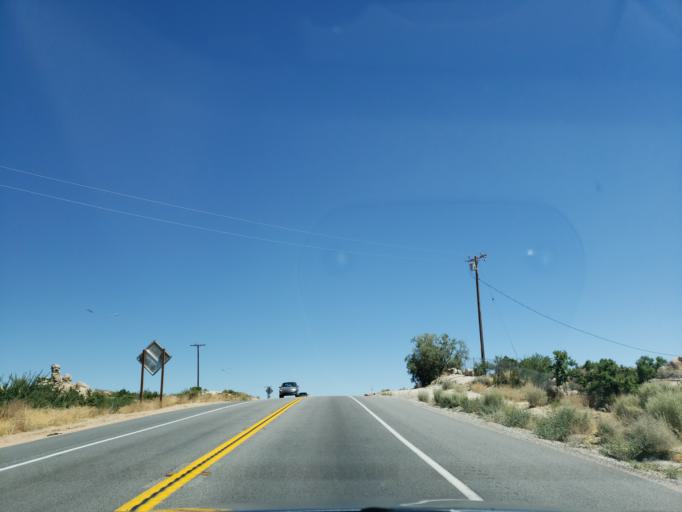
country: US
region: California
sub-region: San Bernardino County
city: Yucca Valley
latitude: 34.1506
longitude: -116.4189
